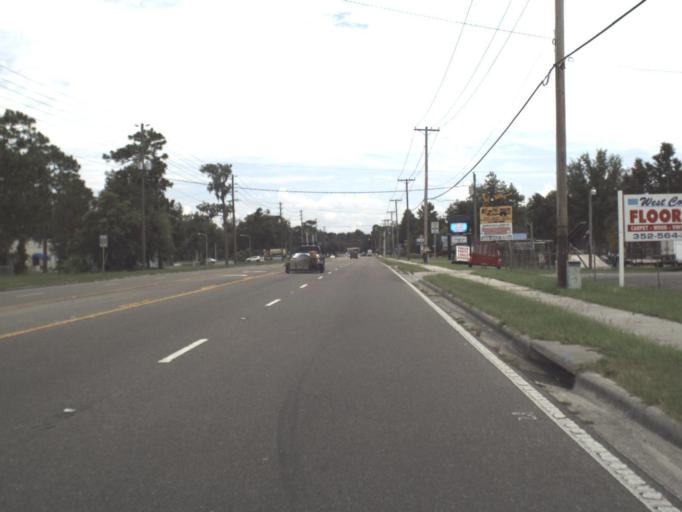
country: US
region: Florida
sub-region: Citrus County
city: Crystal River
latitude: 28.8855
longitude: -82.5438
